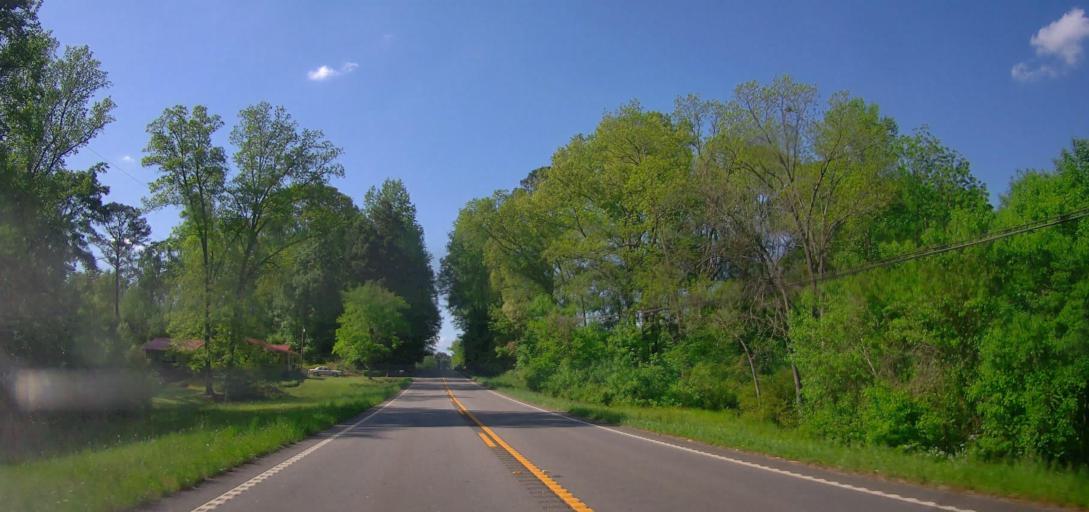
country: US
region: Georgia
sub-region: Morgan County
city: Madison
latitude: 33.6102
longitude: -83.4785
